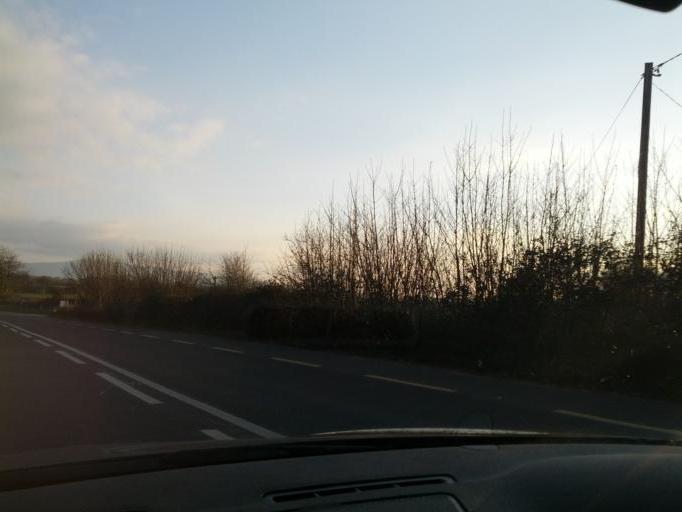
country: IE
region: Munster
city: Nenagh Bridge
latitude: 52.8988
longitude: -8.1871
